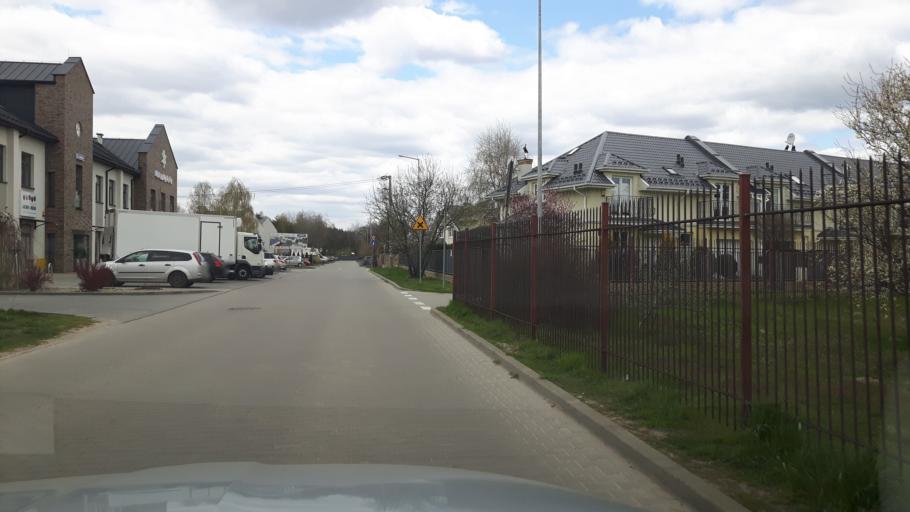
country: PL
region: Masovian Voivodeship
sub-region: Powiat wolominski
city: Kobylka
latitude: 52.3457
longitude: 21.1942
